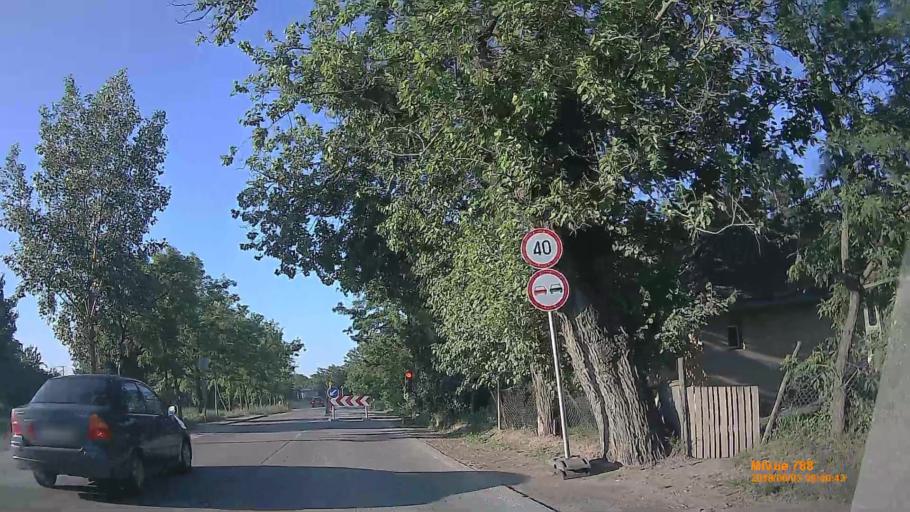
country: HU
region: Pest
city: Delegyhaza
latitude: 47.2760
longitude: 19.1065
